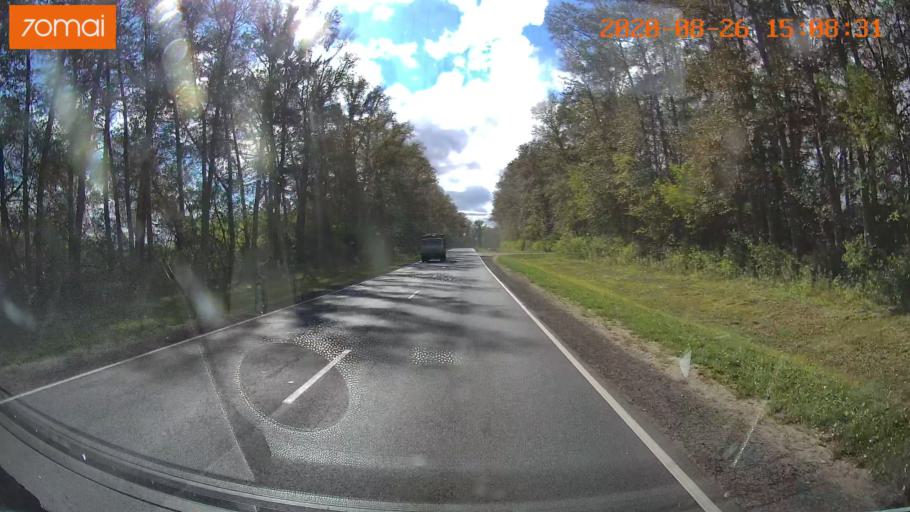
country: RU
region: Rjazan
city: Oktyabr'skiy
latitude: 54.1422
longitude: 38.7023
